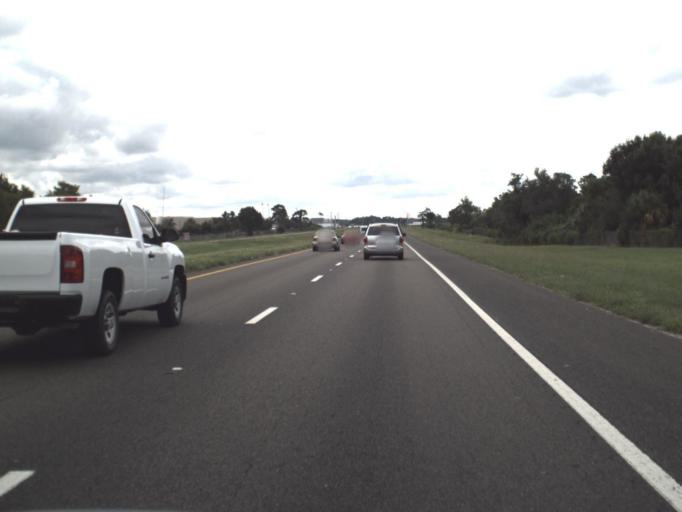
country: US
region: Florida
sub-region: Manatee County
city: Whitfield
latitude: 27.4109
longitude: -82.5331
